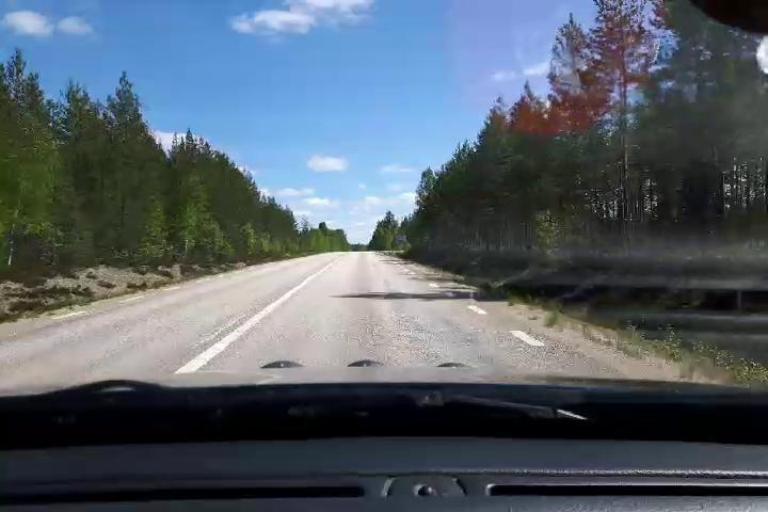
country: SE
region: Gaevleborg
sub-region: Ljusdals Kommun
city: Farila
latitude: 61.9904
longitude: 15.2683
